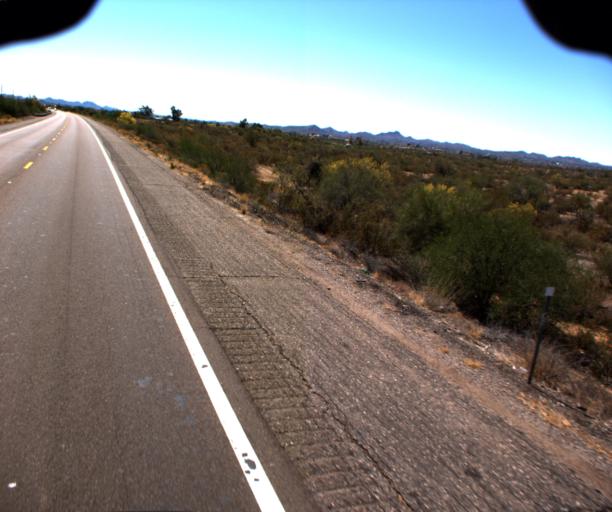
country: US
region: Arizona
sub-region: Maricopa County
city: Wickenburg
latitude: 34.0137
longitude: -112.7929
